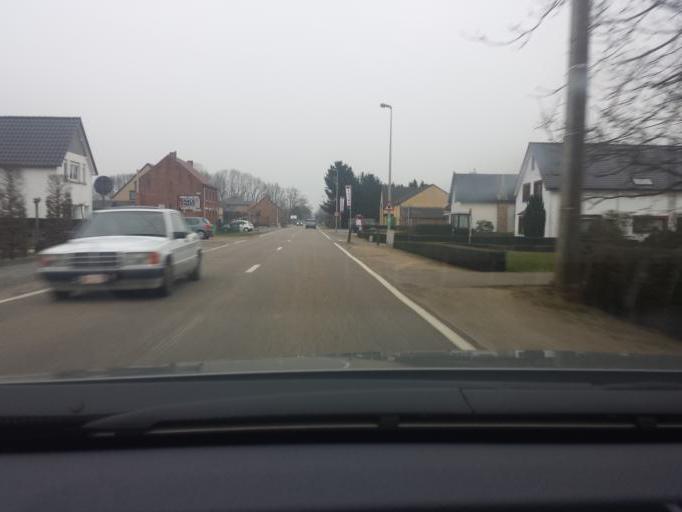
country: BE
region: Flanders
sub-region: Provincie Limburg
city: Lummen
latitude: 51.0041
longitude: 5.1353
